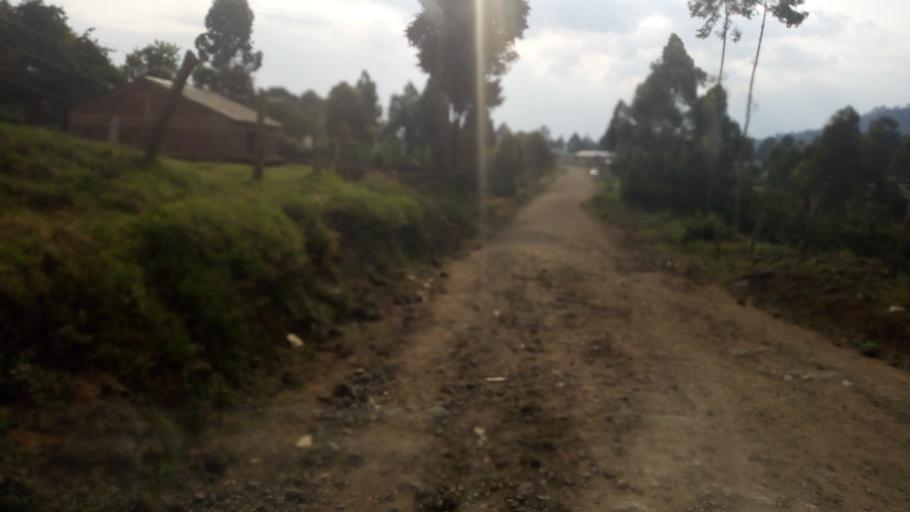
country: UG
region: Western Region
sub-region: Kisoro District
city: Kisoro
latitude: -1.2918
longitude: 29.6967
